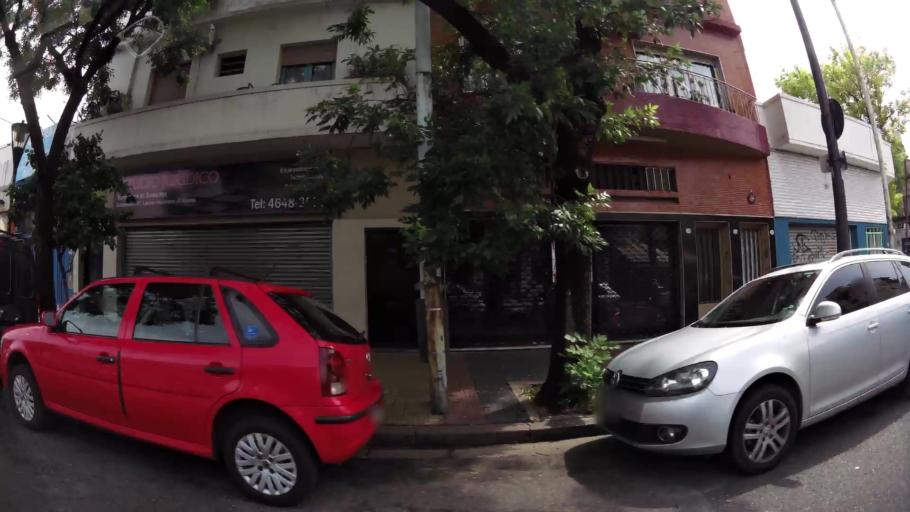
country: AR
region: Buenos Aires F.D.
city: Villa Santa Rita
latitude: -34.6236
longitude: -58.5125
